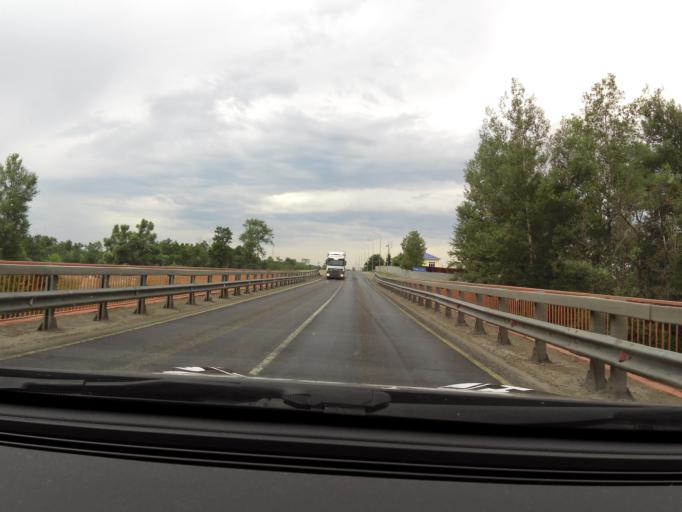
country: RU
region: Bashkortostan
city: Urman
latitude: 54.8259
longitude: 56.8934
